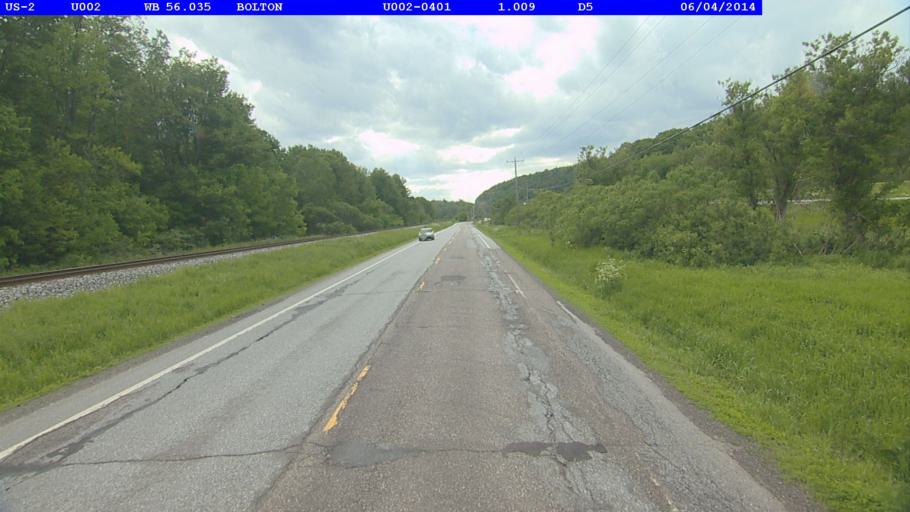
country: US
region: Vermont
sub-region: Chittenden County
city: Jericho
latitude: 44.3797
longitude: -72.9139
